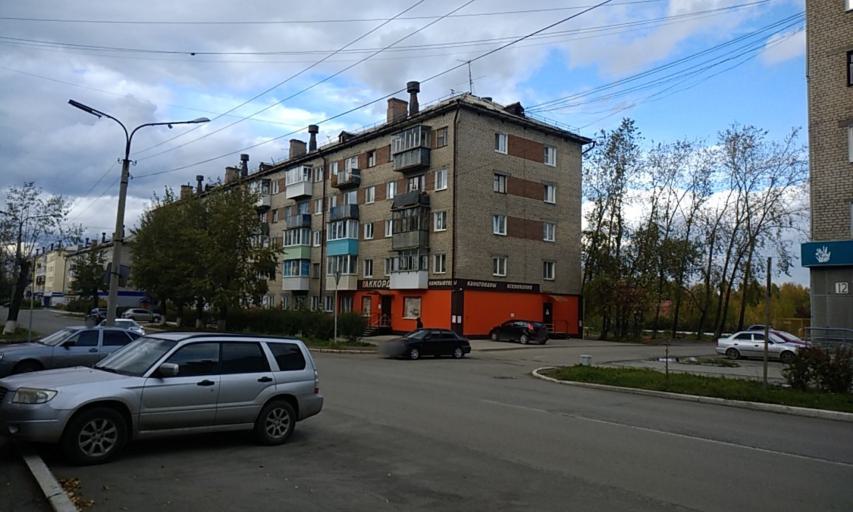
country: RU
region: Sverdlovsk
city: Krasnoural'sk
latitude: 58.3555
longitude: 60.0444
